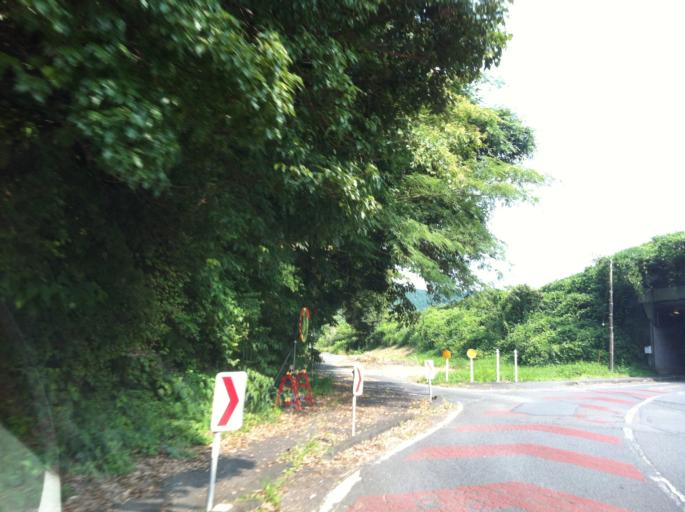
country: JP
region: Shizuoka
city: Shimada
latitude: 34.8489
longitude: 138.1801
